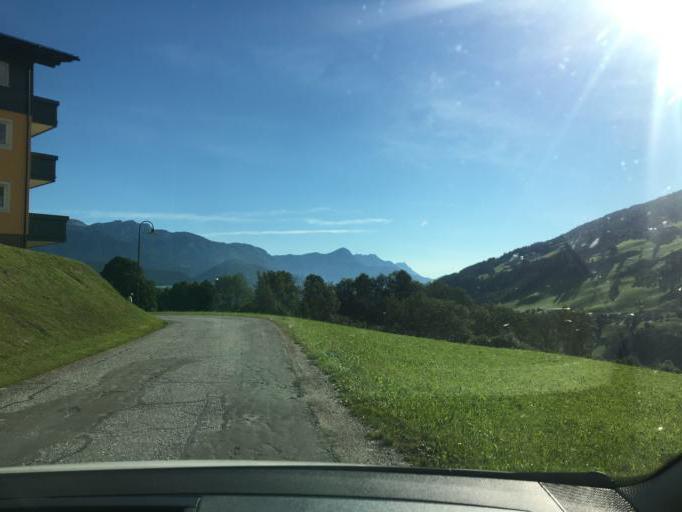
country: AT
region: Styria
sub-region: Politischer Bezirk Liezen
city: Schladming
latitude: 47.3804
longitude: 13.6718
